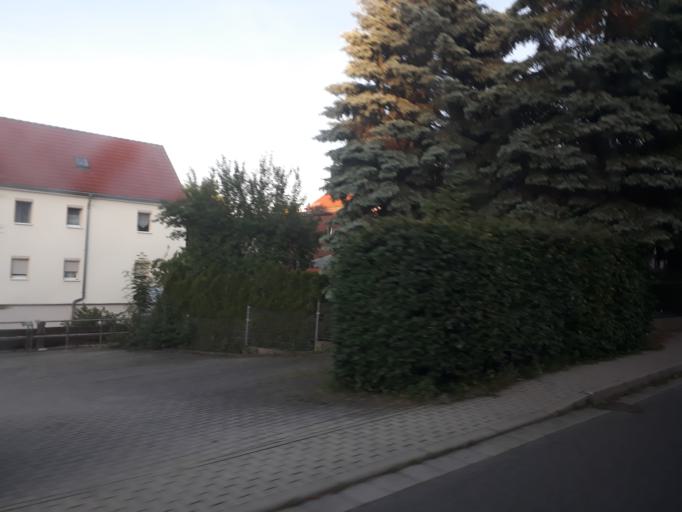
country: DE
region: Saxony
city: Radeberg
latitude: 51.0579
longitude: 13.8862
